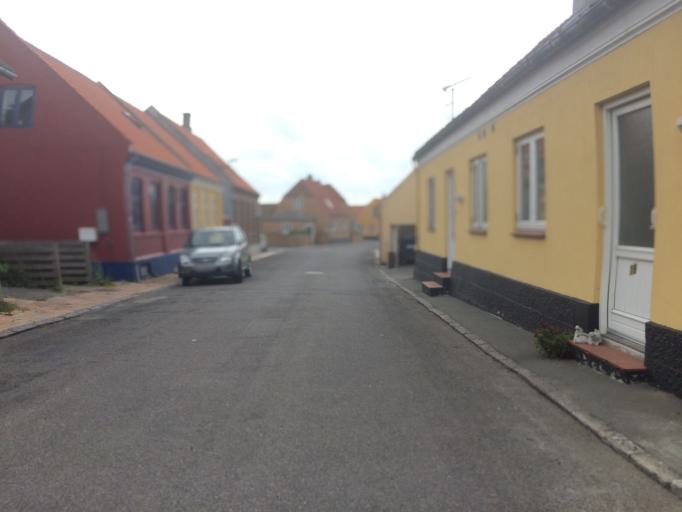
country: DK
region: Capital Region
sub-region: Bornholm Kommune
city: Ronne
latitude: 55.1835
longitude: 14.7077
